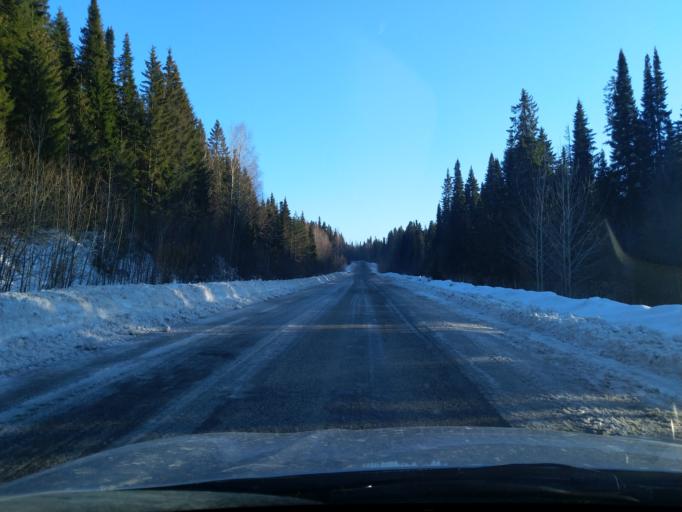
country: RU
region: Perm
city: Polazna
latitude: 58.3021
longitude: 56.4738
